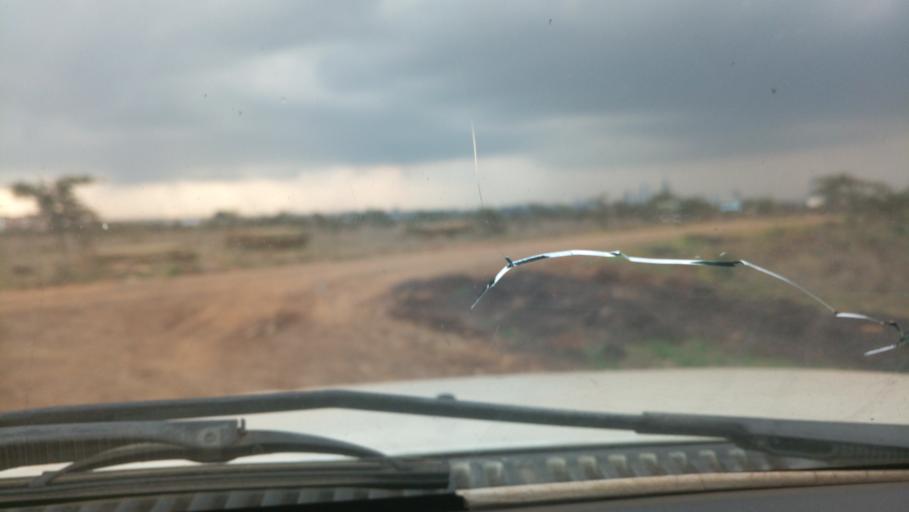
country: KE
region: Nairobi Area
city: Nairobi
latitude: -1.3343
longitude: 36.8236
